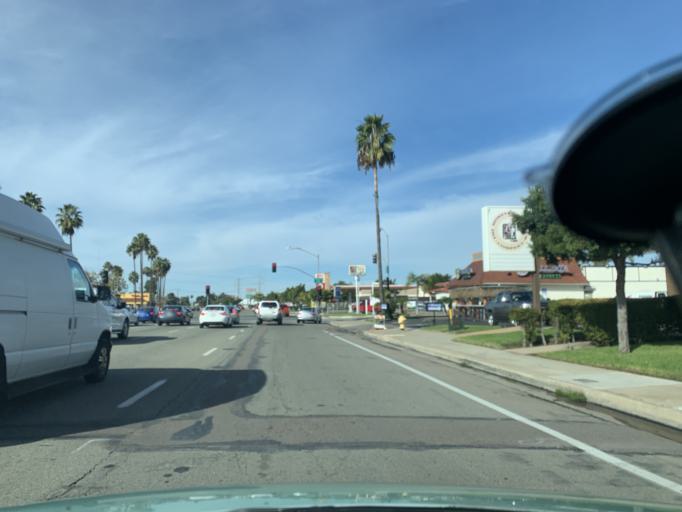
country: US
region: California
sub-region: San Diego County
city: La Jolla
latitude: 32.8209
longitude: -117.1826
